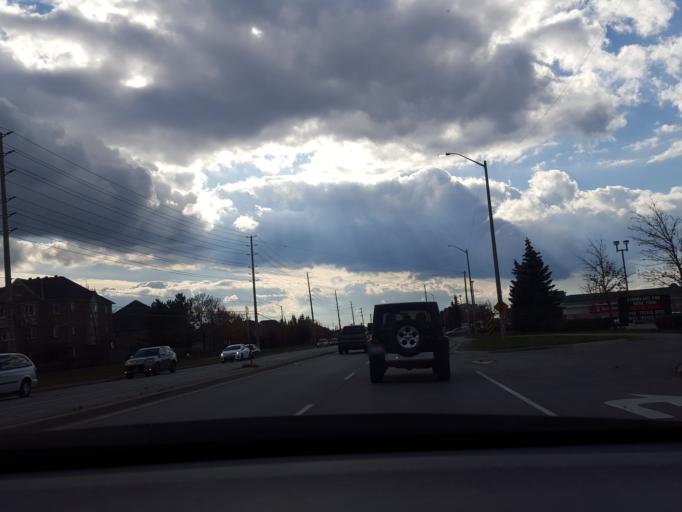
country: CA
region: Ontario
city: Brampton
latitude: 43.5832
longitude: -79.7771
